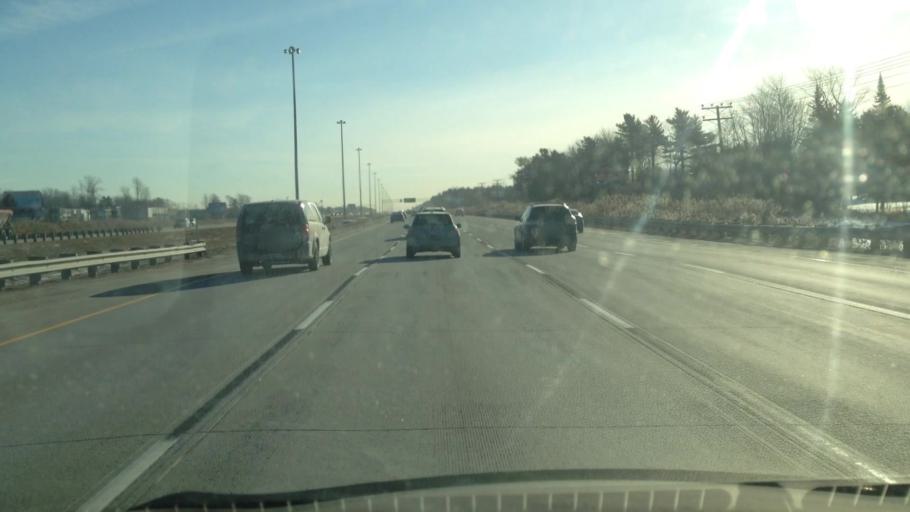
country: CA
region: Quebec
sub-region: Laurentides
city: Blainville
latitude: 45.6723
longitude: -73.9078
